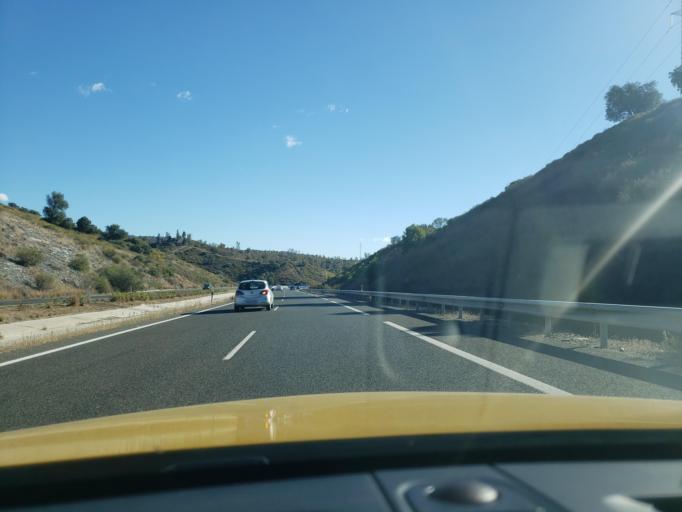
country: ES
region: Andalusia
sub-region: Provincia de Malaga
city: Ojen
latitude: 36.5148
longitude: -4.7939
